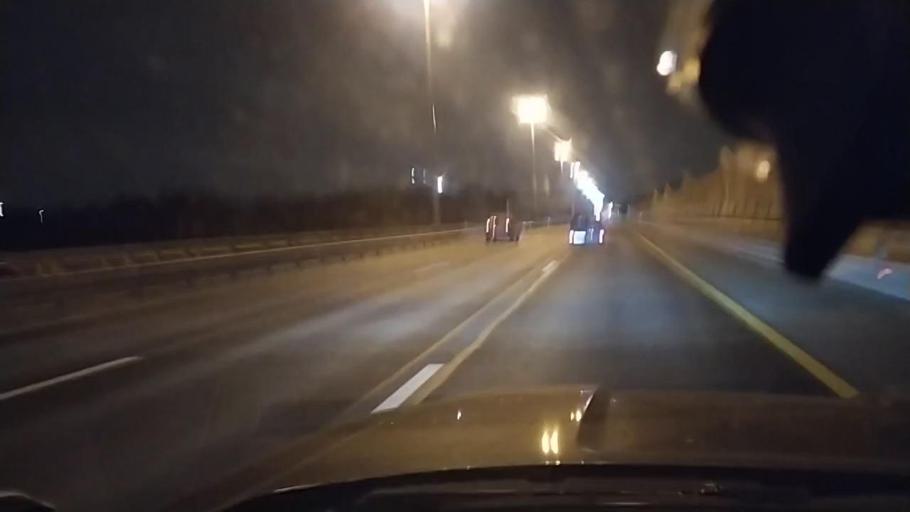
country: RU
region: Leningrad
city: Untolovo
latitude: 60.0348
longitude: 30.1858
